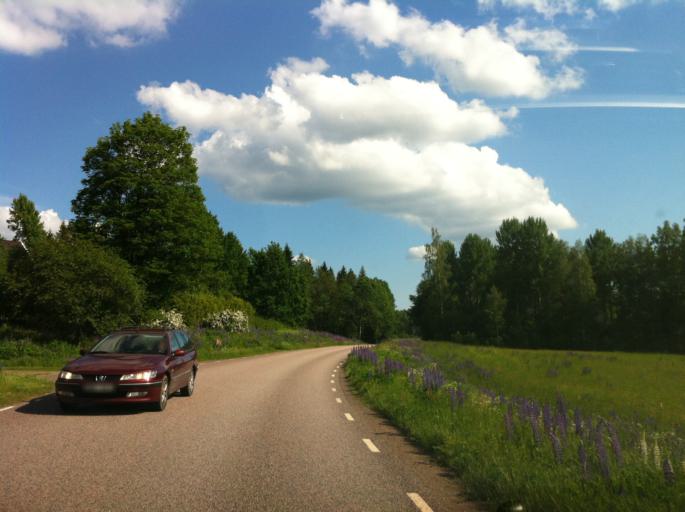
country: SE
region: Vaermland
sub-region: Kils Kommun
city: Kil
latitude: 59.6698
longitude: 13.2904
